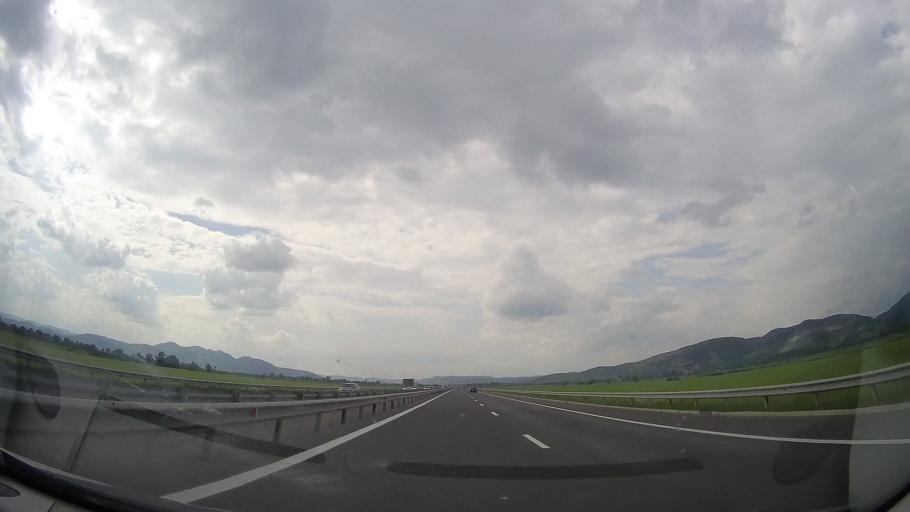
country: RO
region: Hunedoara
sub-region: Oras Simeria
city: Simeria
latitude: 45.8738
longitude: 23.0090
